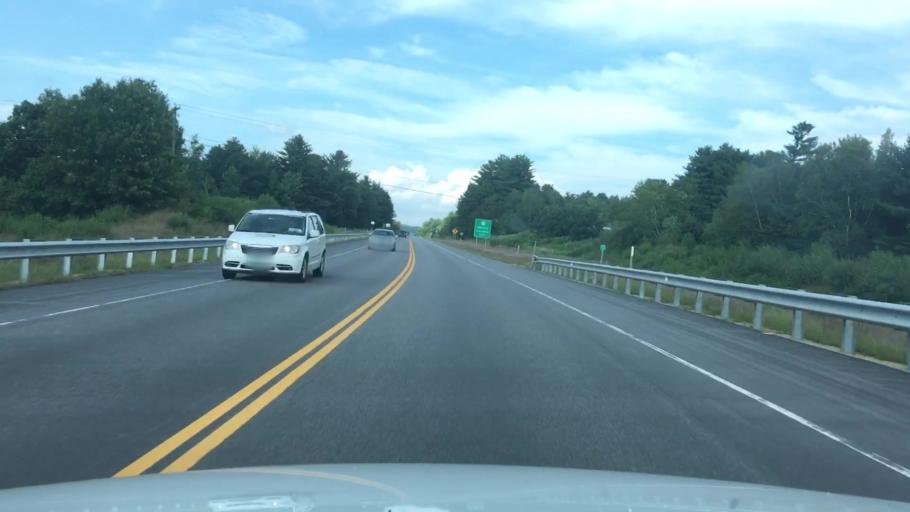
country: US
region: New Hampshire
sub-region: Belknap County
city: Laconia
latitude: 43.5141
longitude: -71.4532
